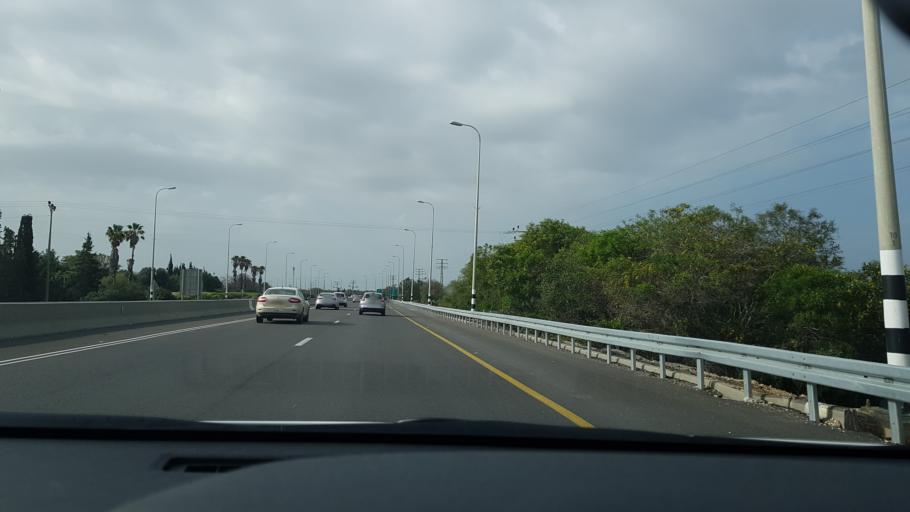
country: IL
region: Southern District
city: Ashqelon
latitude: 31.6514
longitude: 34.5972
